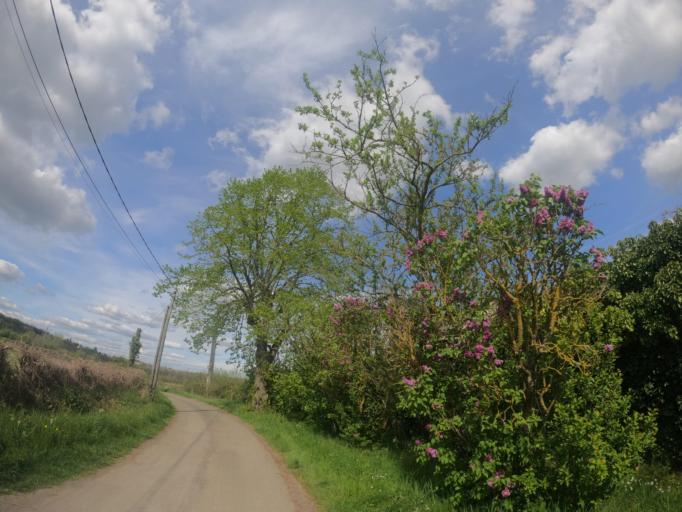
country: FR
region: Poitou-Charentes
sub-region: Departement des Deux-Sevres
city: Saint-Jean-de-Thouars
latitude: 46.9198
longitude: -0.1910
